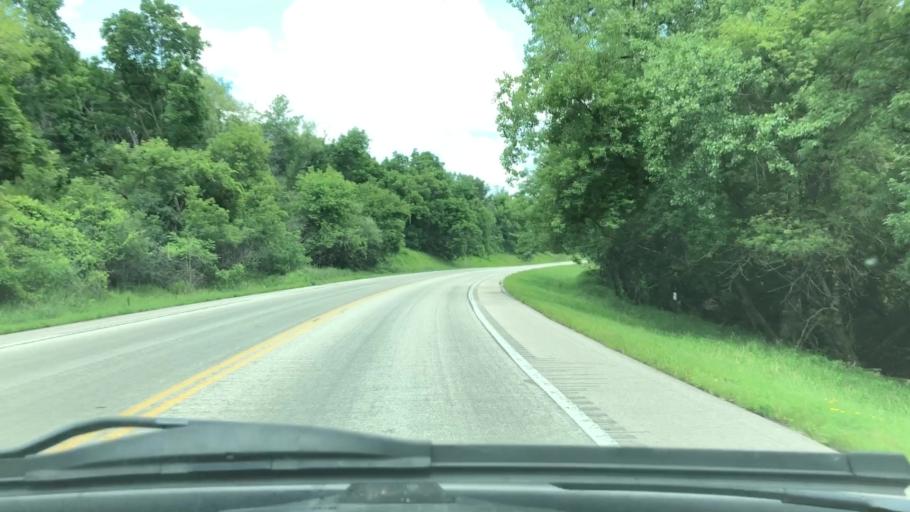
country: US
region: Minnesota
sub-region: Olmsted County
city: Rochester
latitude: 43.9824
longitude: -92.5092
